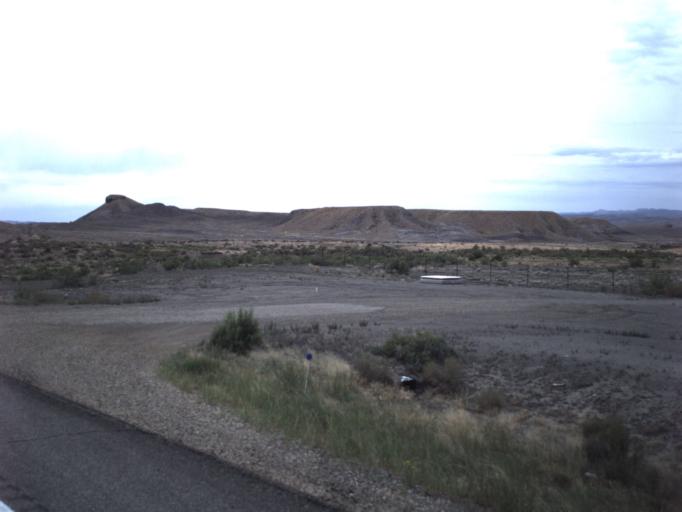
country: US
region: Utah
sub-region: Carbon County
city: East Carbon City
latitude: 39.3483
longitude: -110.3780
